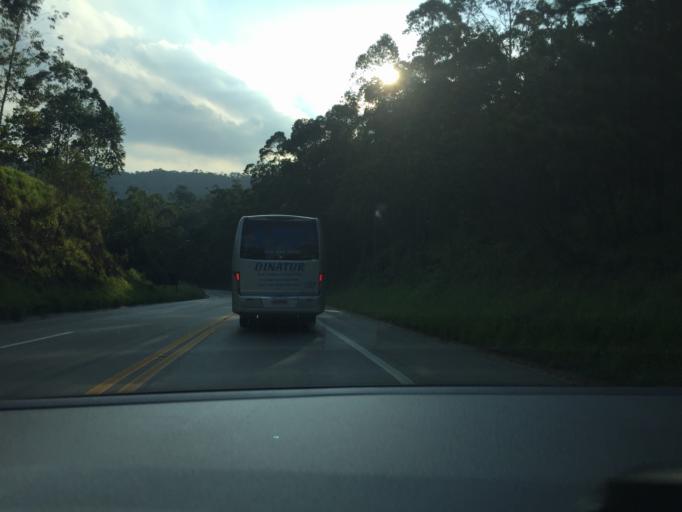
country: BR
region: Sao Paulo
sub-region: Francisco Morato
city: Francisco Morato
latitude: -23.2641
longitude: -46.7957
